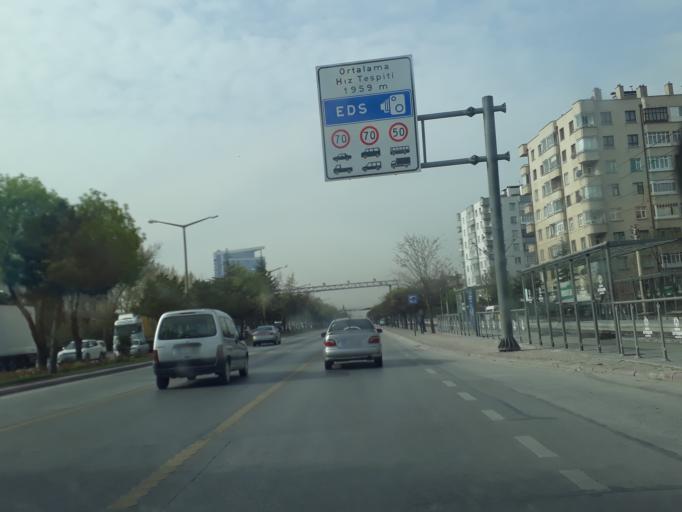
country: TR
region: Konya
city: Selcuklu
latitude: 37.9408
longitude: 32.5116
